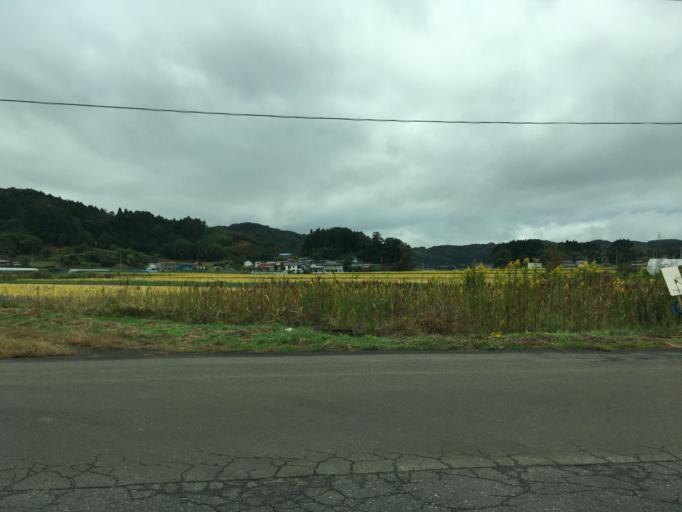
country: JP
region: Fukushima
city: Nihommatsu
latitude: 37.6172
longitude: 140.4358
